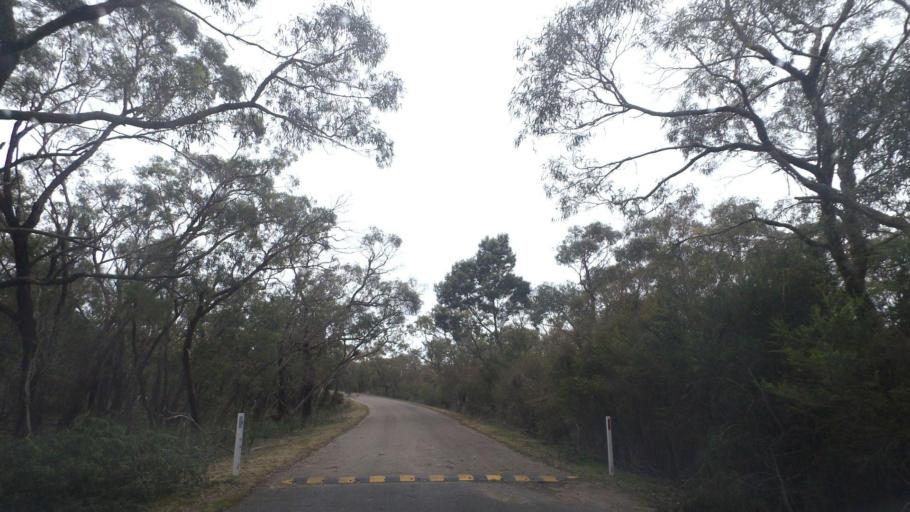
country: AU
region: Victoria
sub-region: Casey
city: Botanic Ridge
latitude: -38.1347
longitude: 145.2823
